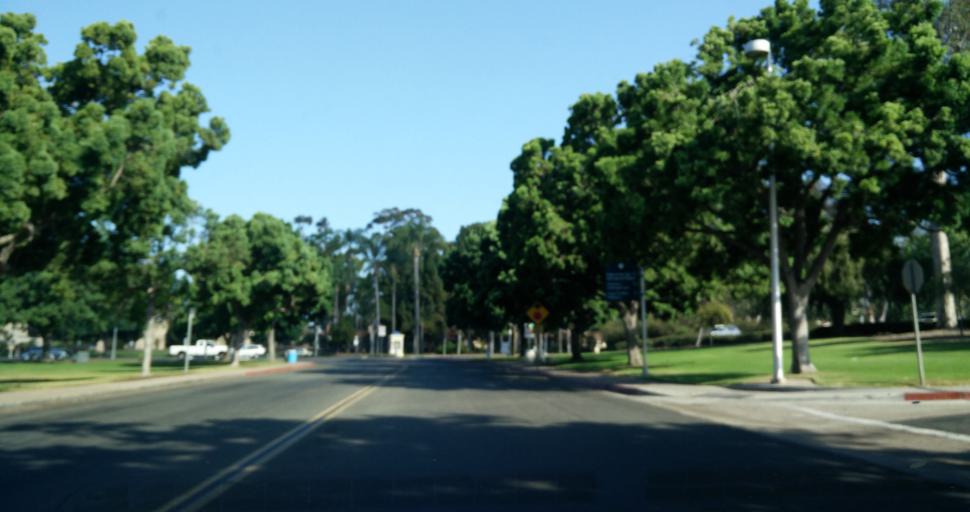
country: US
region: California
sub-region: San Diego County
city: San Diego
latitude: 32.7276
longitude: -117.1515
